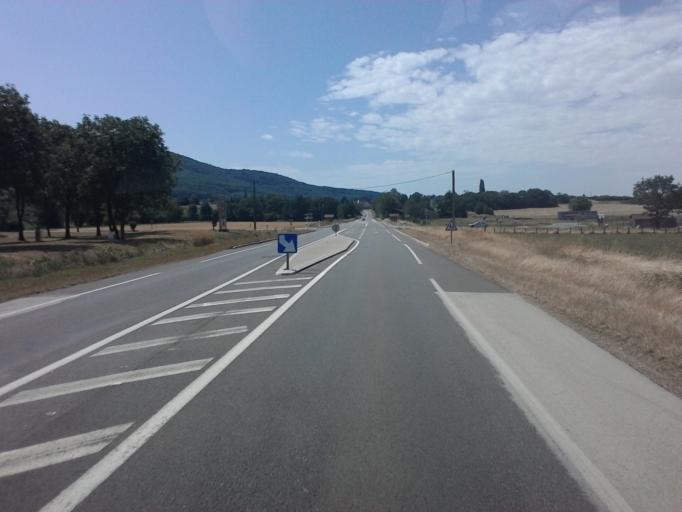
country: FR
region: Franche-Comte
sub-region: Departement du Jura
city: Cousance
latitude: 46.5838
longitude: 5.4439
